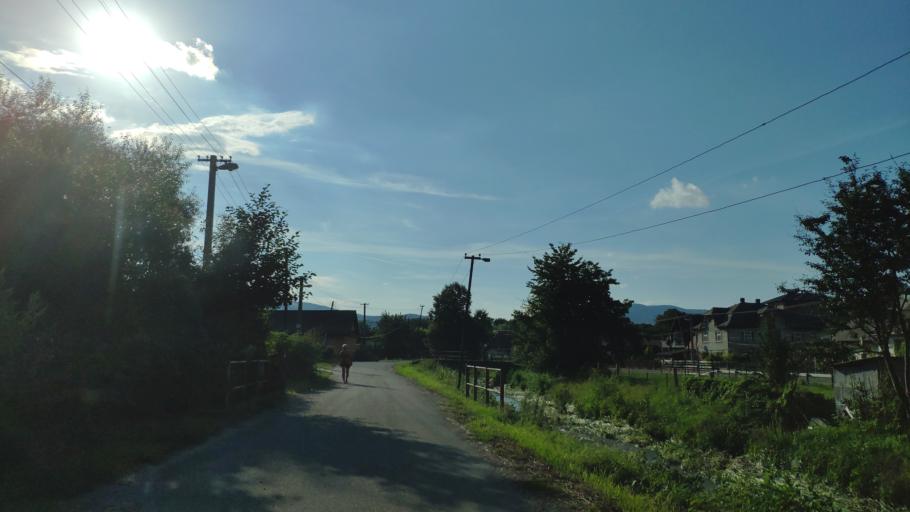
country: SK
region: Kosicky
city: Secovce
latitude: 48.6125
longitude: 21.5304
